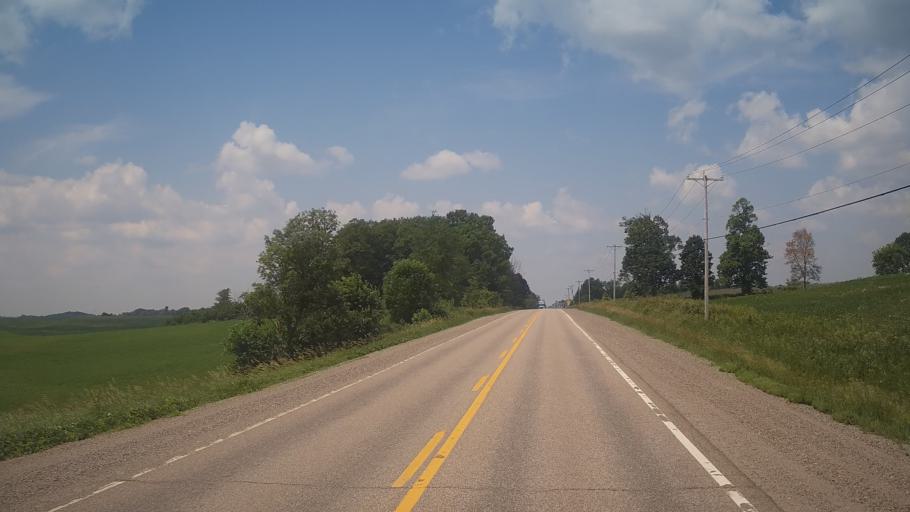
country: CA
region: Quebec
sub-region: Outaouais
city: Shawville
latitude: 45.5925
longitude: -76.4745
